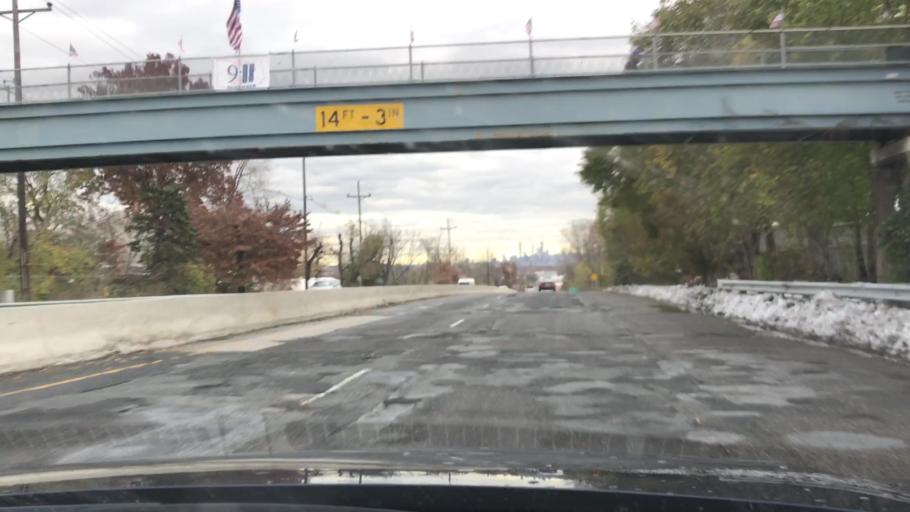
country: US
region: New Jersey
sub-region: Bergen County
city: Hasbrouck Heights
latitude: 40.8706
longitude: -74.0668
